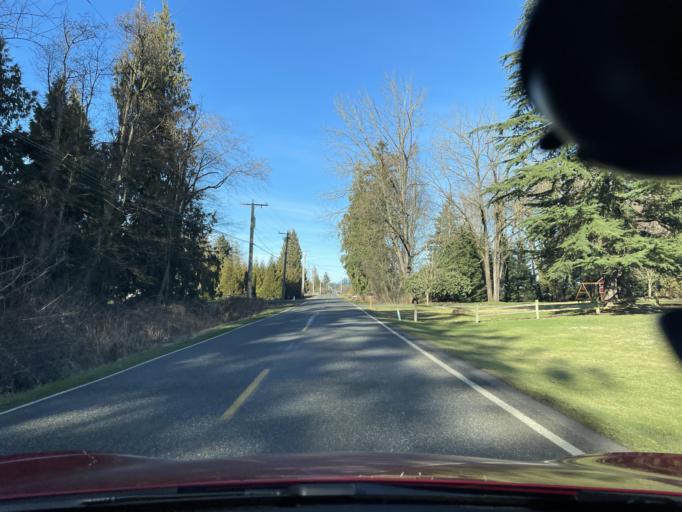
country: US
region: Washington
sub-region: Whatcom County
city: Lynden
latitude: 48.9577
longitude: -122.5303
